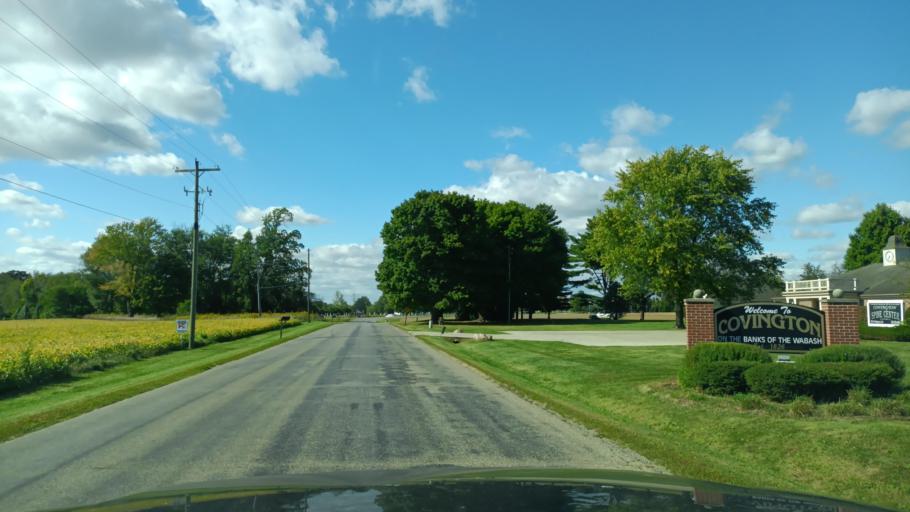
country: US
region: Indiana
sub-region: Fountain County
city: Covington
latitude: 40.1264
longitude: -87.3836
